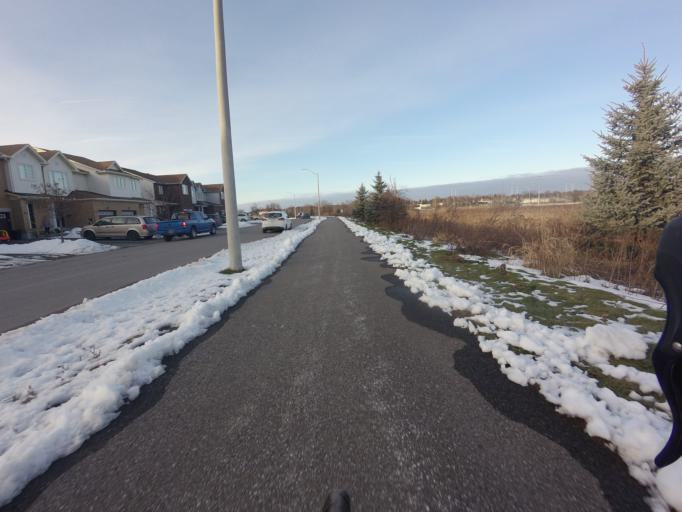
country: CA
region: Ontario
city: Bells Corners
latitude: 45.2753
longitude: -75.8621
